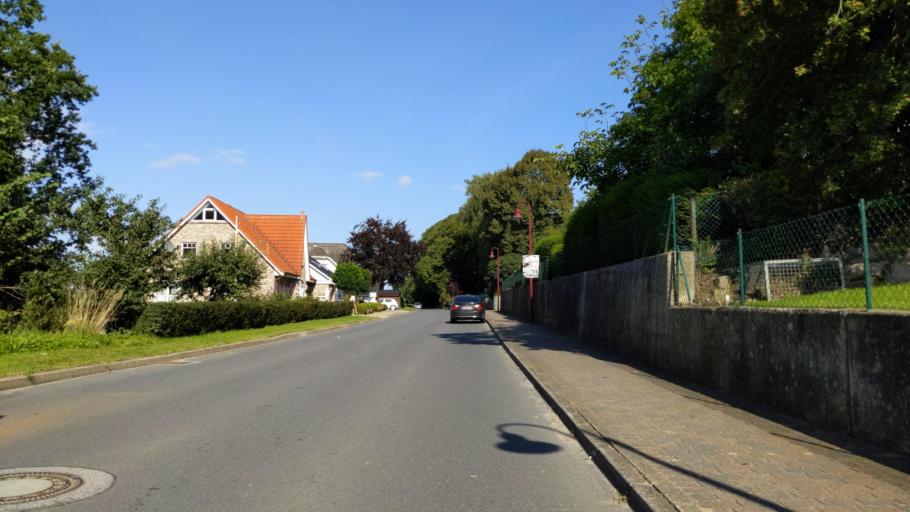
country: DE
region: Schleswig-Holstein
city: Stockelsdorf
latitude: 53.9515
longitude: 10.6231
